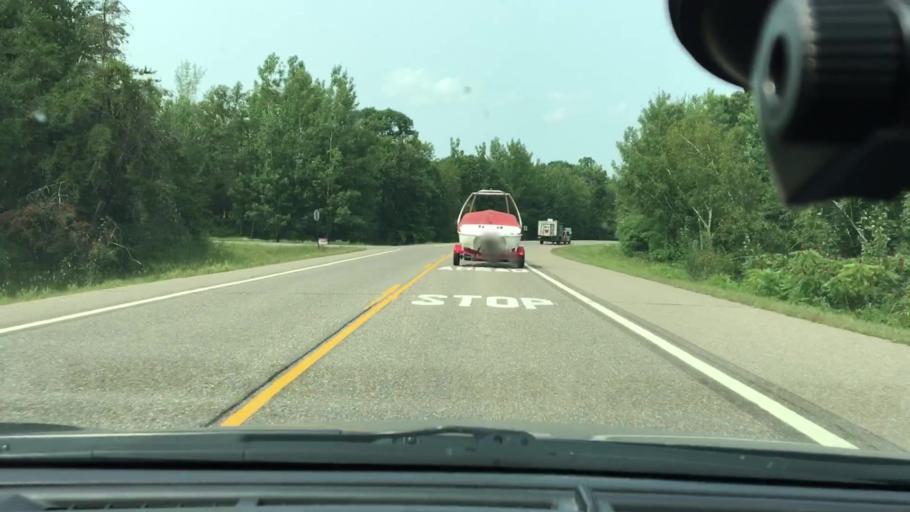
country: US
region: Minnesota
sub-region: Cass County
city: East Gull Lake
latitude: 46.4064
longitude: -94.3547
